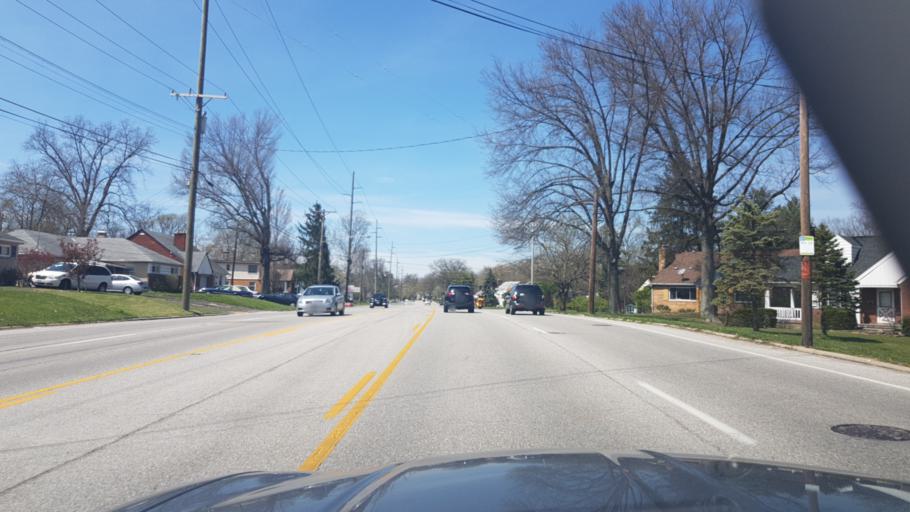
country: US
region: Ohio
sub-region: Hamilton County
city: Fruit Hill
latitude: 39.0756
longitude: -84.3644
